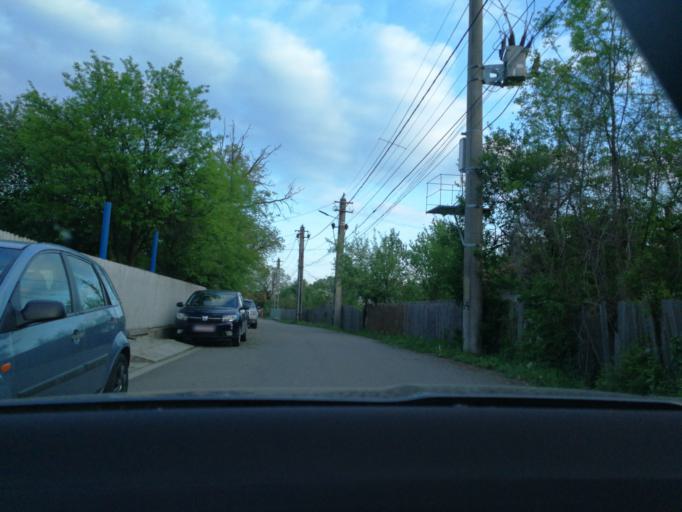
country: RO
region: Prahova
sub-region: Comuna Cornu
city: Cornu de Jos
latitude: 45.1568
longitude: 25.6975
